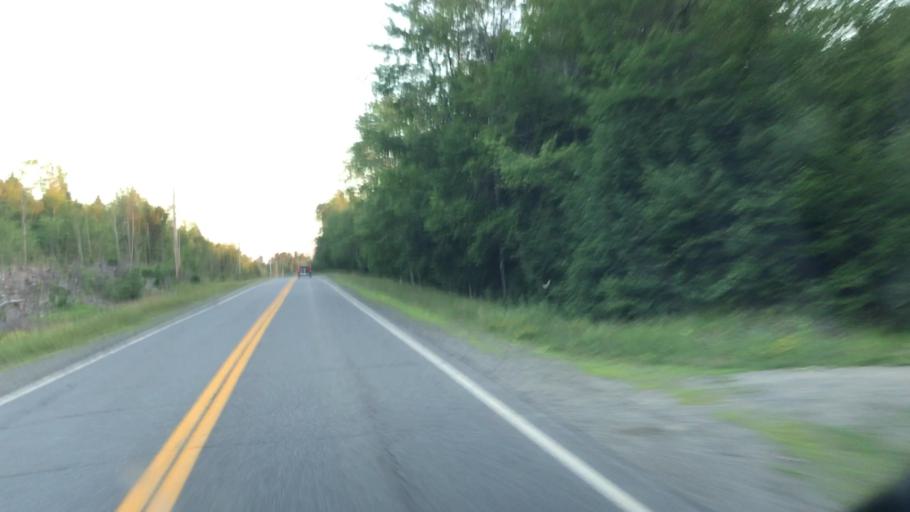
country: US
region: Maine
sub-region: Penobscot County
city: Medway
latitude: 45.5944
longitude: -68.3117
